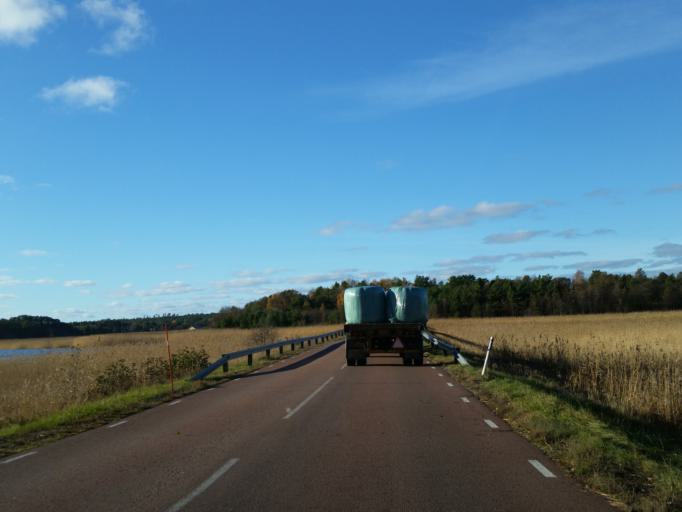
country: AX
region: Alands landsbygd
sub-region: Geta
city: Geta
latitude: 60.3658
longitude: 19.7792
